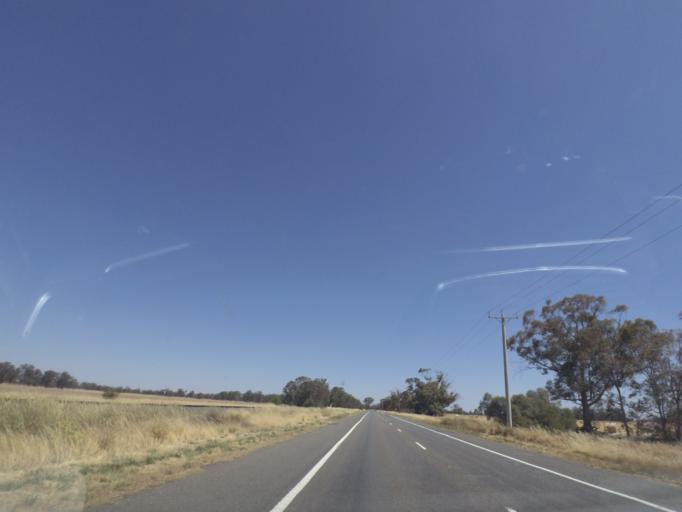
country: AU
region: Victoria
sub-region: Greater Shepparton
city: Shepparton
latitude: -36.2210
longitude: 145.4318
